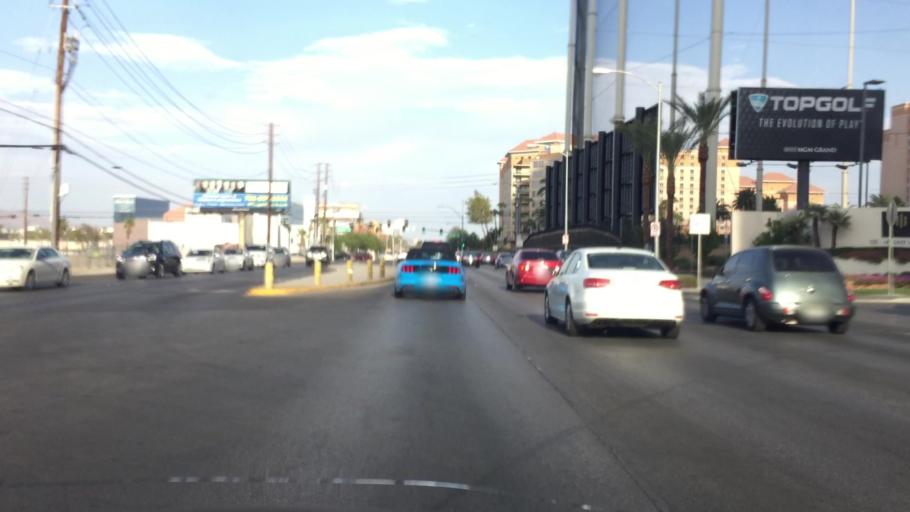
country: US
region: Nevada
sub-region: Clark County
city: Paradise
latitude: 36.1080
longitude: -115.1659
